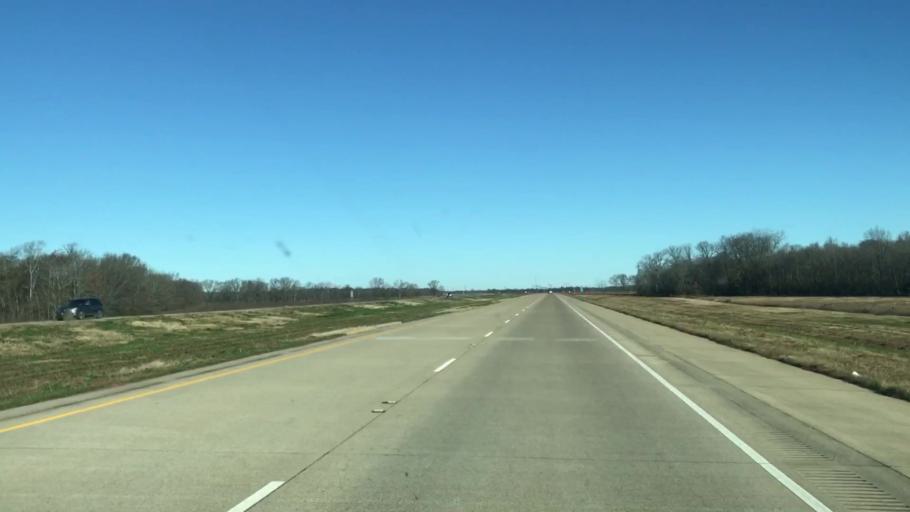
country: US
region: Louisiana
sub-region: Caddo Parish
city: Blanchard
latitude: 32.6414
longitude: -93.8385
